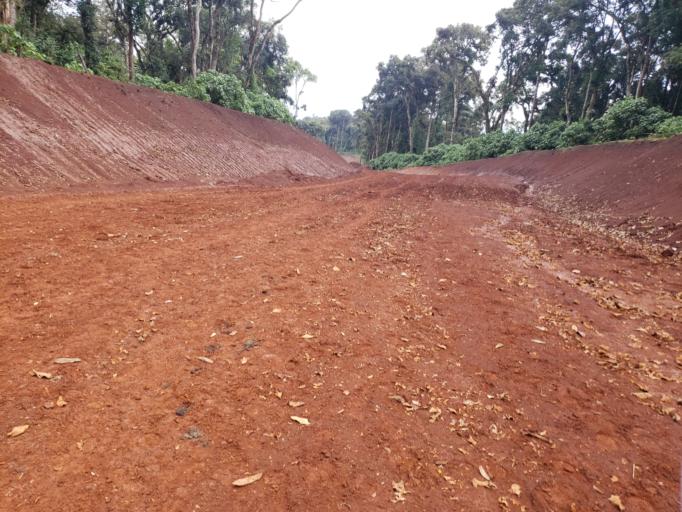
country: ET
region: Oromiya
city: Dodola
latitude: 6.5923
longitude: 39.4121
